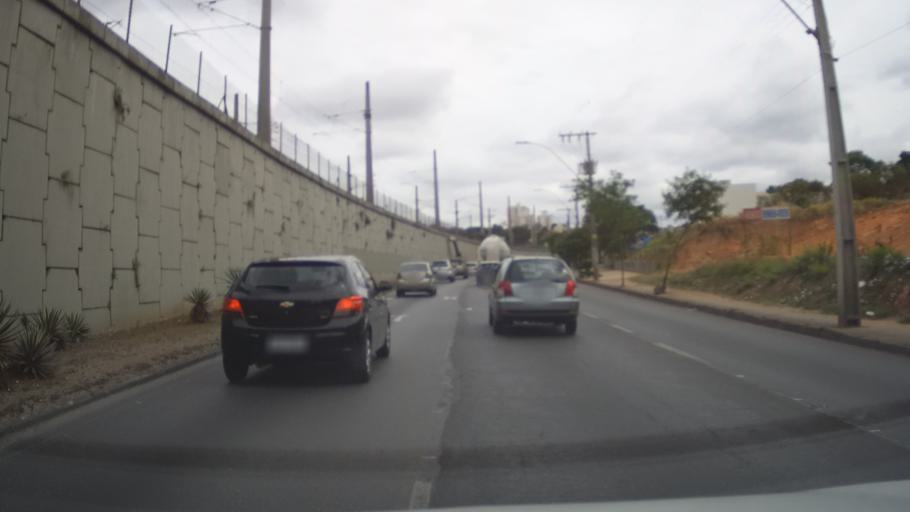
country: BR
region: Minas Gerais
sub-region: Belo Horizonte
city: Belo Horizonte
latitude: -19.8560
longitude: -43.9350
